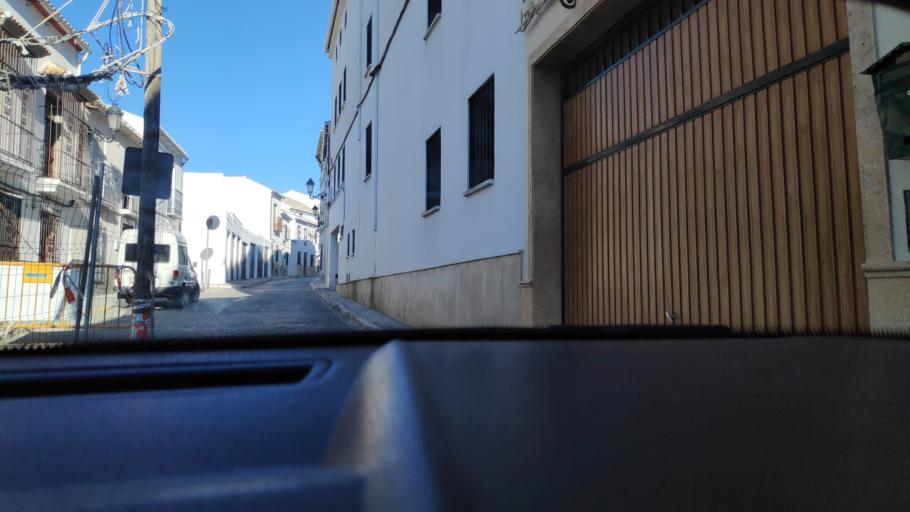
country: ES
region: Andalusia
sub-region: Province of Cordoba
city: Baena
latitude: 37.6136
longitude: -4.3312
